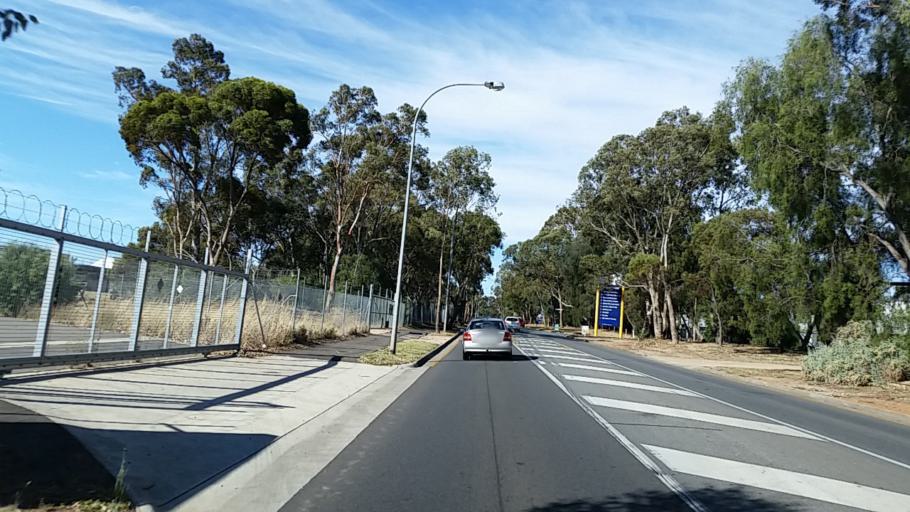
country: AU
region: South Australia
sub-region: Salisbury
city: Salisbury
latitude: -34.7814
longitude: 138.6401
